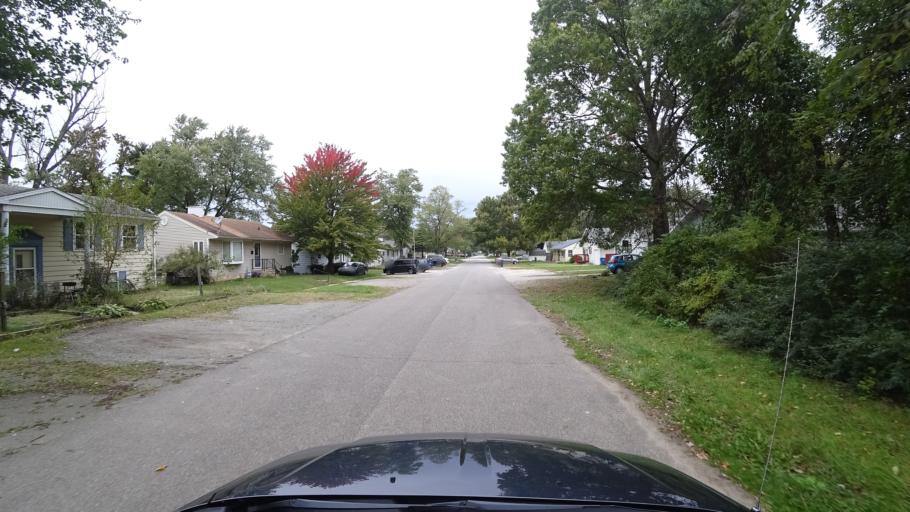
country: US
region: Indiana
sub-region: LaPorte County
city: Michigan City
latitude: 41.6963
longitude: -86.9024
